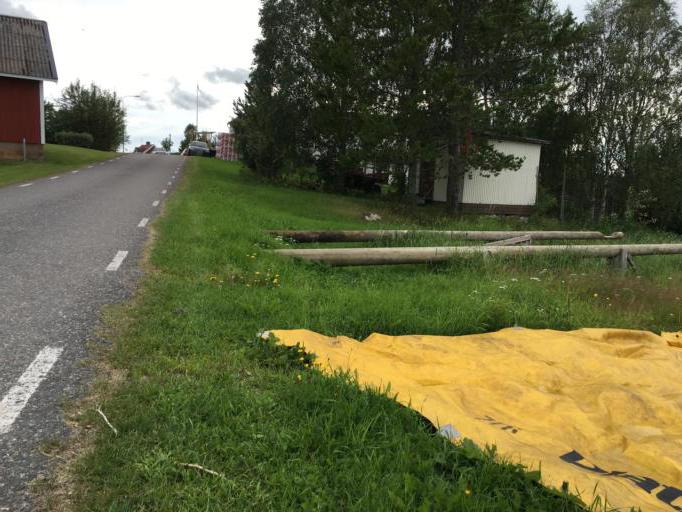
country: SE
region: Norrbotten
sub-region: Overkalix Kommun
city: OEverkalix
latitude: 66.1074
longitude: 22.7845
